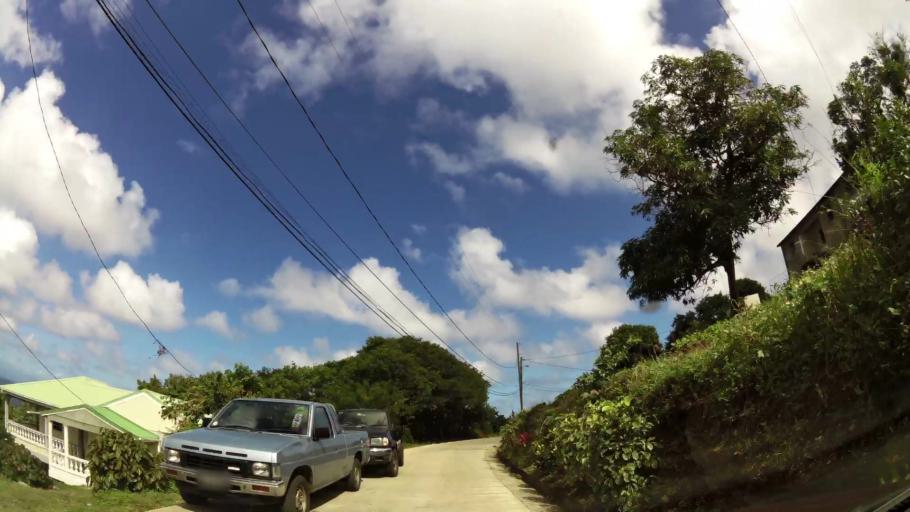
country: DM
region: Saint John
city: Portsmouth
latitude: 15.6345
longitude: -61.4597
